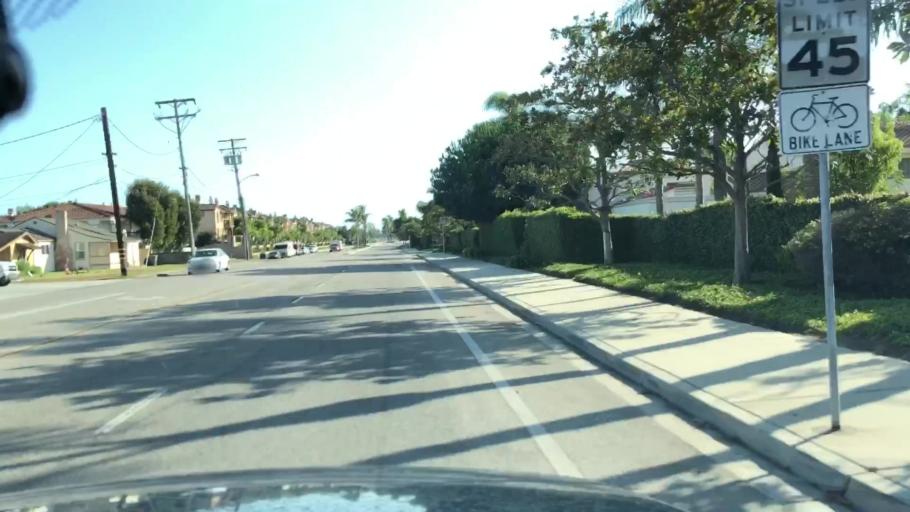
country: US
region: California
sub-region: Ventura County
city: Oxnard
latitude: 34.1901
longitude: -119.2081
